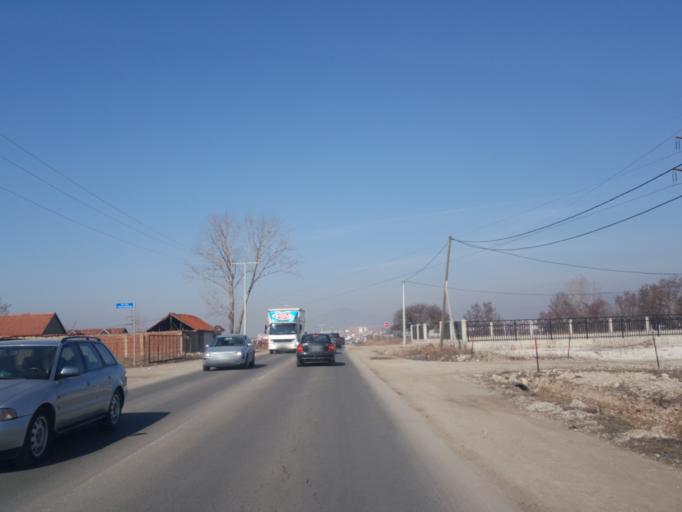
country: XK
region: Mitrovica
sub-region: Vushtrri
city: Vushtrri
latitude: 42.8017
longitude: 20.9941
